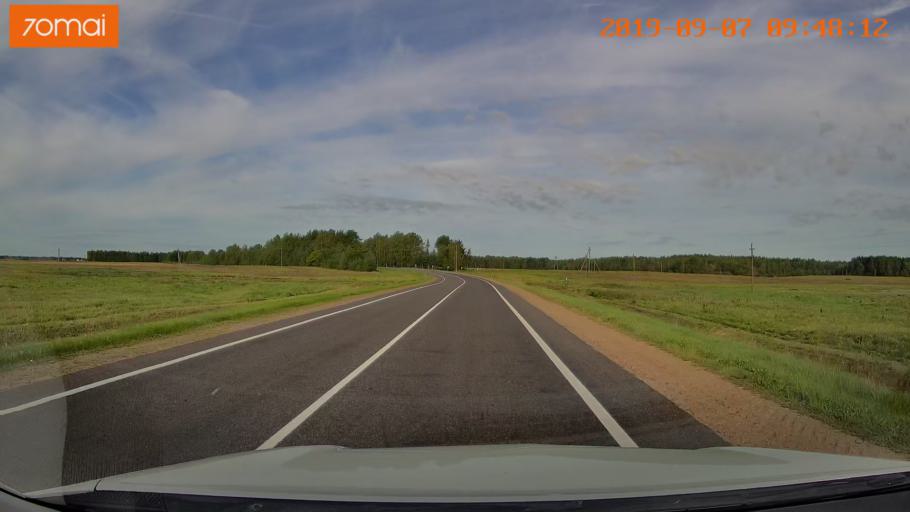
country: BY
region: Grodnenskaya
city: Iwye
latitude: 53.9757
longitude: 25.6916
